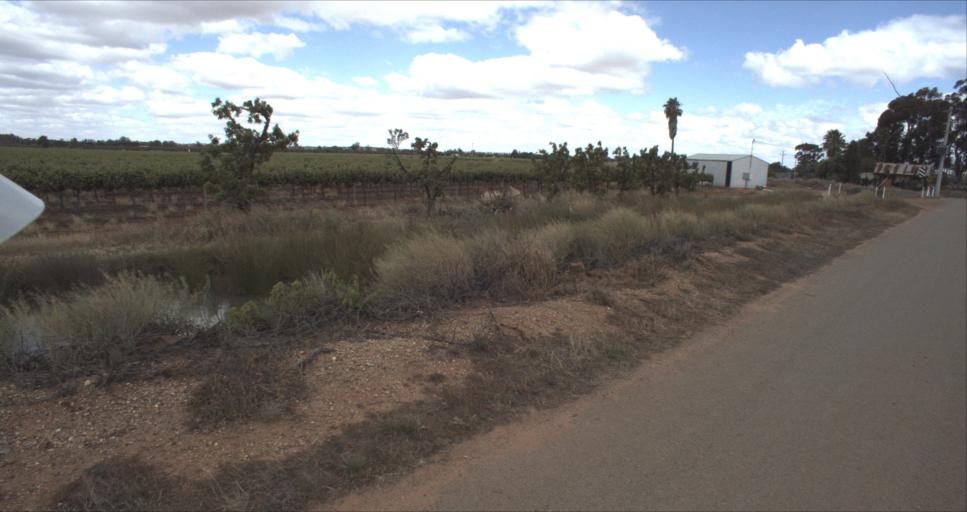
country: AU
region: New South Wales
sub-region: Leeton
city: Leeton
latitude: -34.5792
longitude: 146.4003
